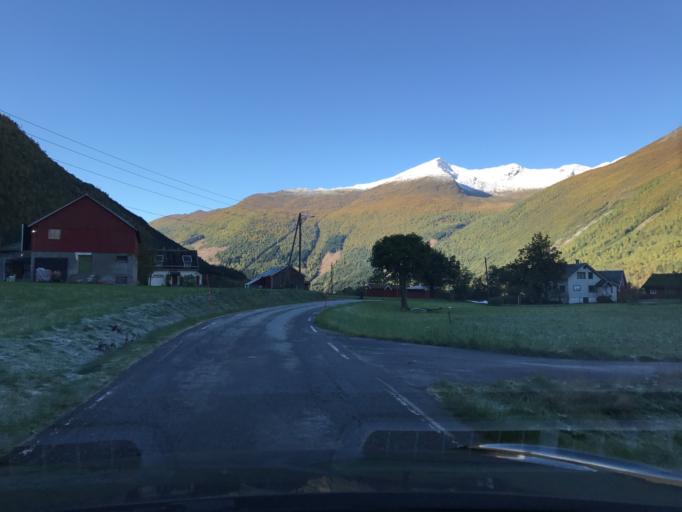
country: NO
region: More og Romsdal
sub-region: Norddal
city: Valldal
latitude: 62.3137
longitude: 7.3077
